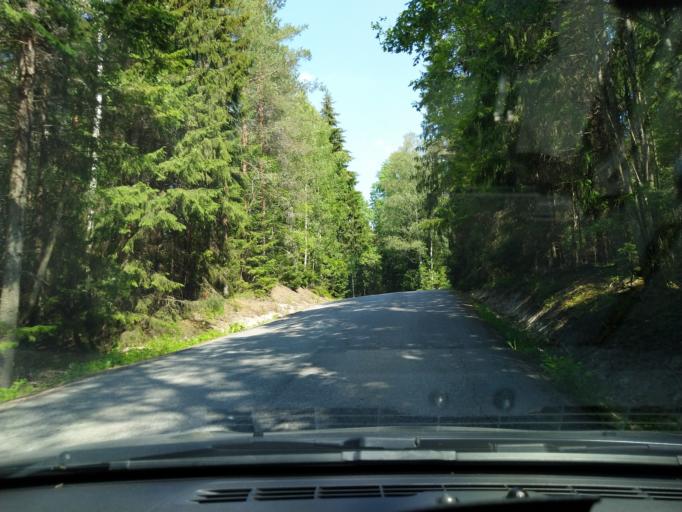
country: FI
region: Uusimaa
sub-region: Helsinki
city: Lohja
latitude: 60.3523
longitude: 24.0889
